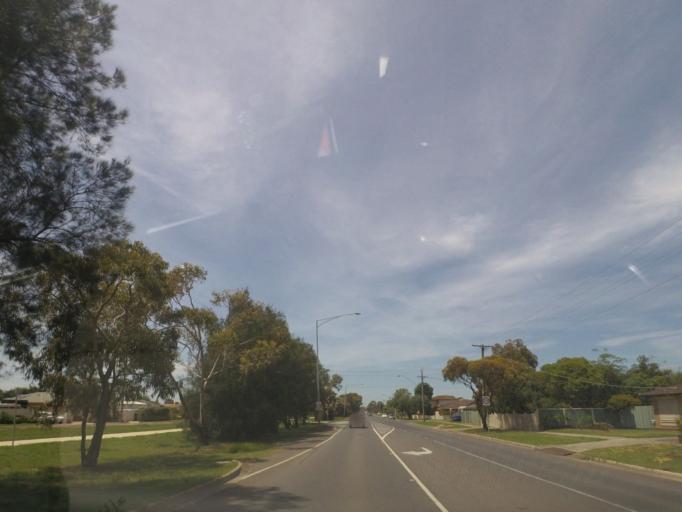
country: AU
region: Victoria
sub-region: Wyndham
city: Werribee
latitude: -37.8864
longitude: 144.6260
